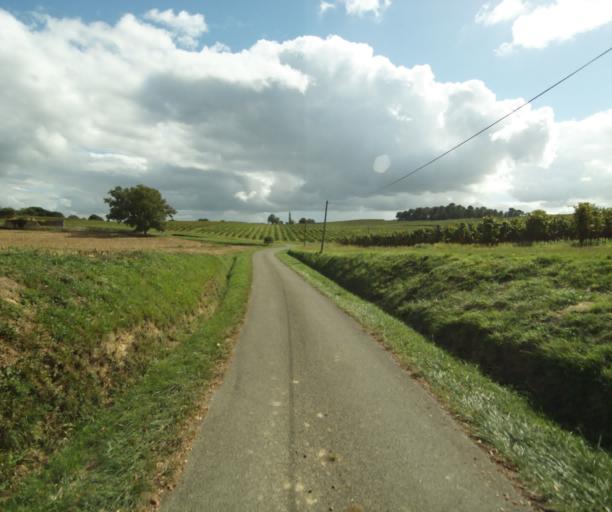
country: FR
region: Midi-Pyrenees
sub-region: Departement du Gers
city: Cazaubon
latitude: 43.8508
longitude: -0.0327
